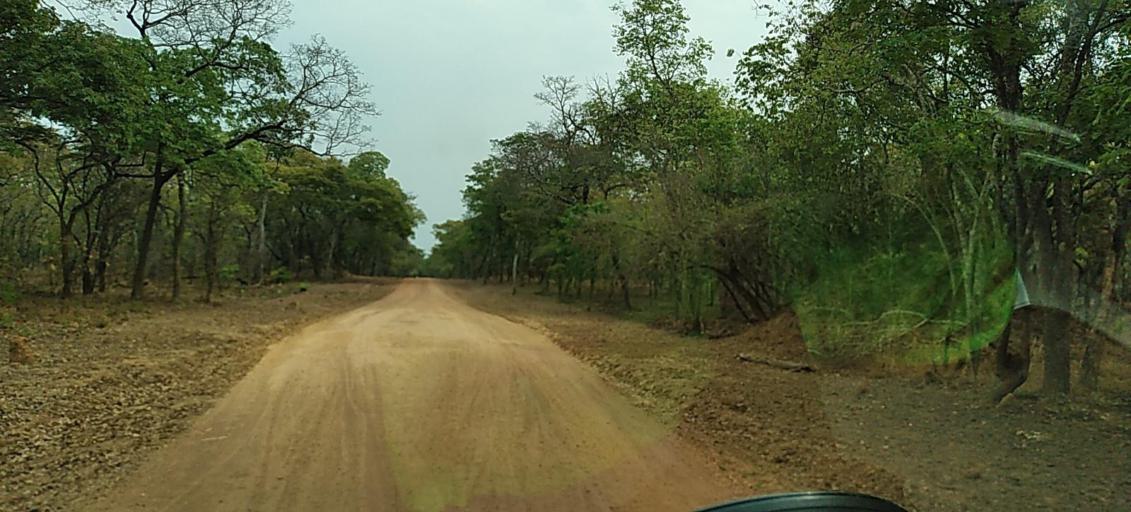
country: ZM
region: North-Western
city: Solwezi
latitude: -12.9243
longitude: 26.5615
